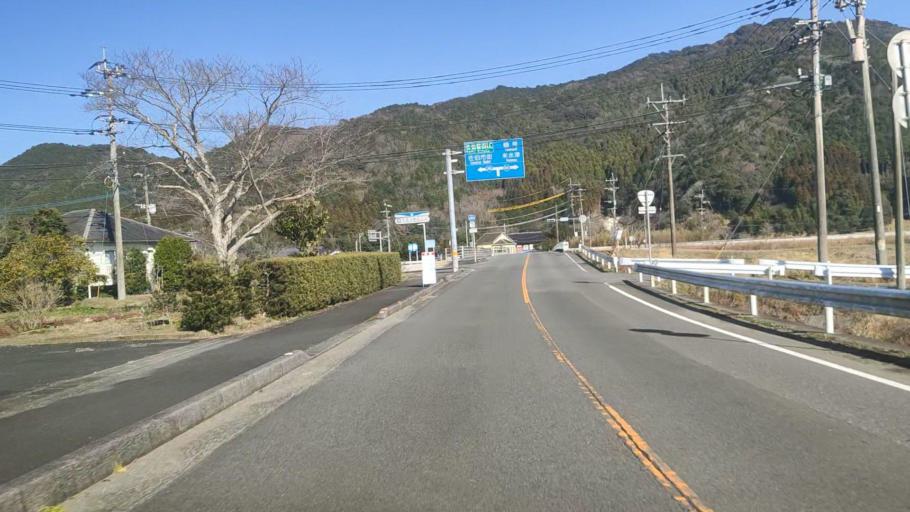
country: JP
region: Oita
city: Saiki
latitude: 32.9311
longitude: 131.9218
